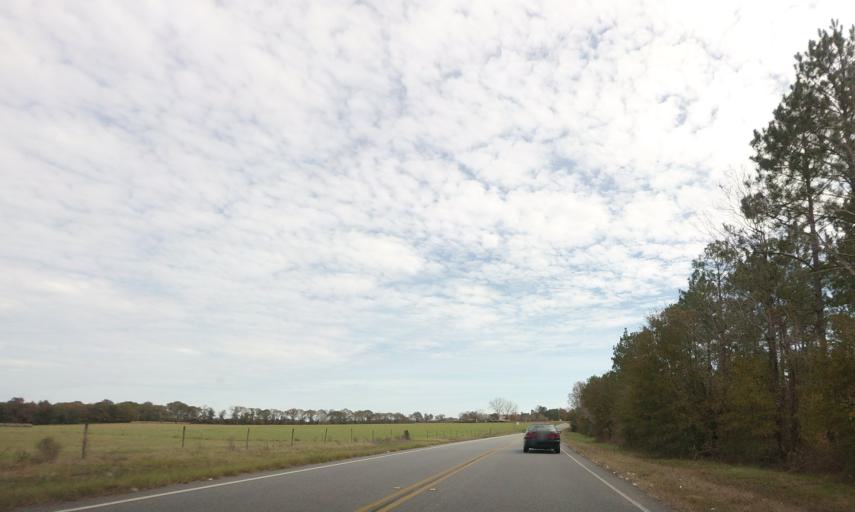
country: US
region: Georgia
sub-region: Dodge County
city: Chester
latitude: 32.4101
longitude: -83.2303
